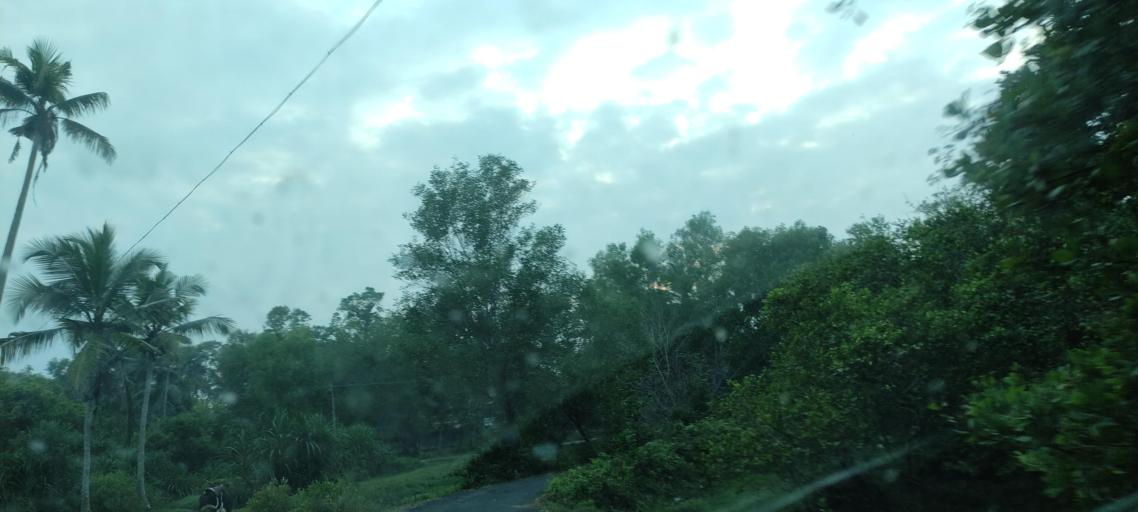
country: IN
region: Kerala
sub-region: Alappuzha
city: Shertallai
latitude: 9.6671
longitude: 76.3565
